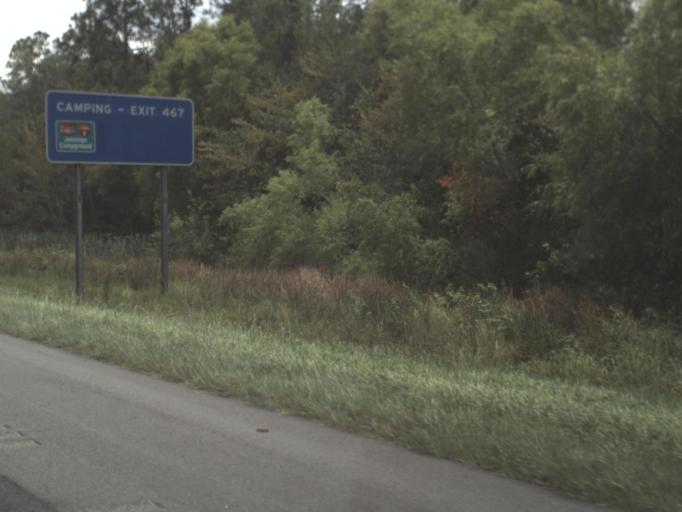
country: US
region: Georgia
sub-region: Echols County
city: Statenville
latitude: 30.6045
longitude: -83.1301
